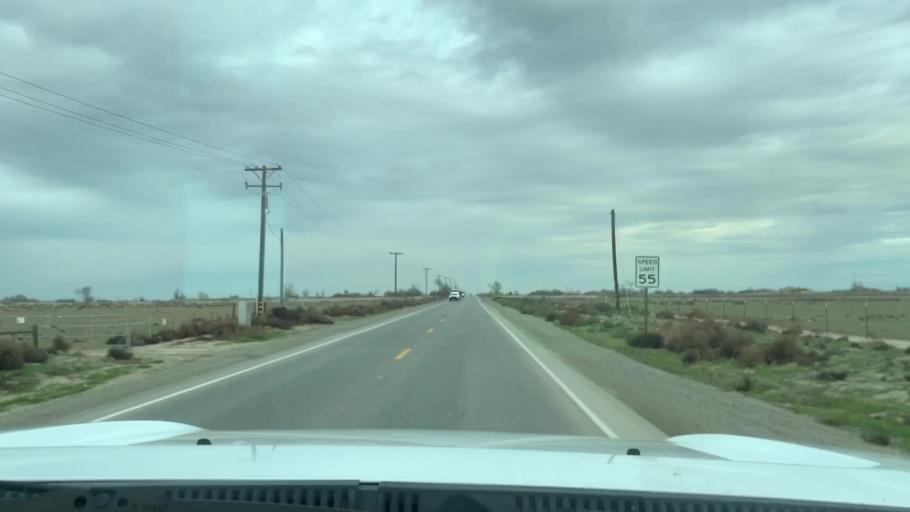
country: US
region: California
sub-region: Kern County
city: Rosedale
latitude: 35.2985
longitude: -119.2524
